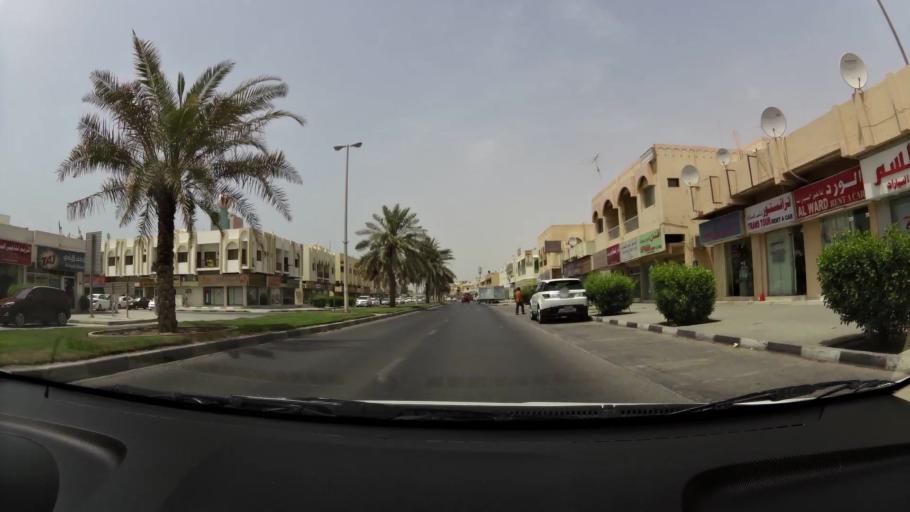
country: AE
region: Ash Shariqah
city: Sharjah
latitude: 25.3505
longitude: 55.4001
